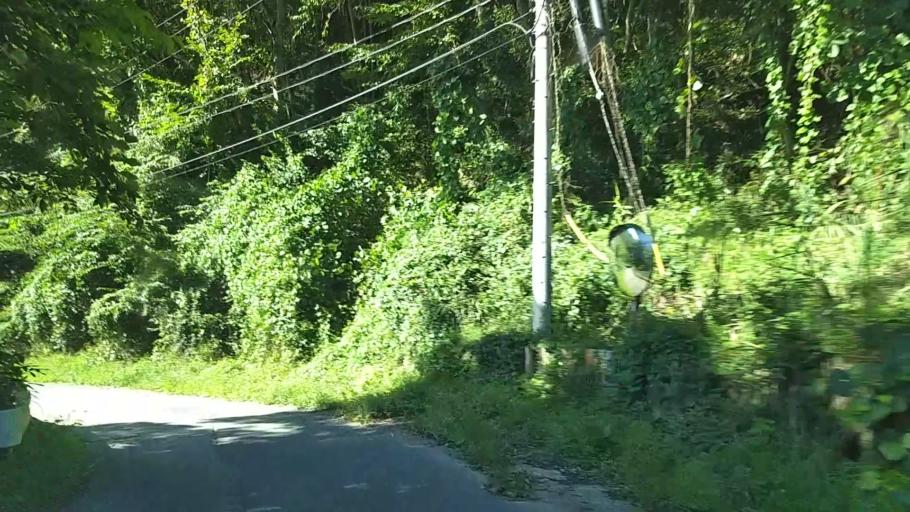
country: JP
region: Nagano
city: Nagano-shi
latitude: 36.5905
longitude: 138.0857
